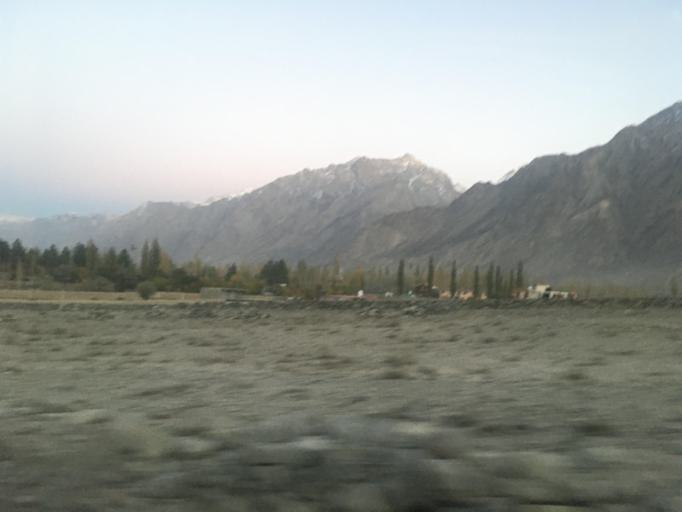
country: PK
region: Gilgit-Baltistan
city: Skardu
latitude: 35.2929
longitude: 75.5698
